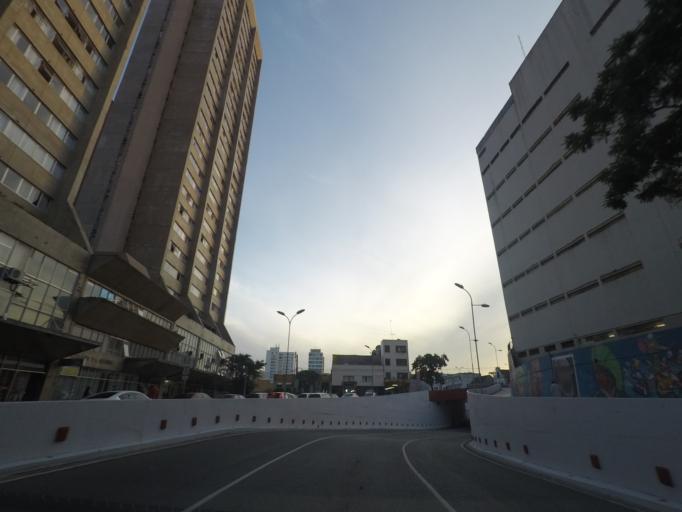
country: BR
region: Parana
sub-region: Curitiba
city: Curitiba
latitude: -25.4286
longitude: -49.2733
